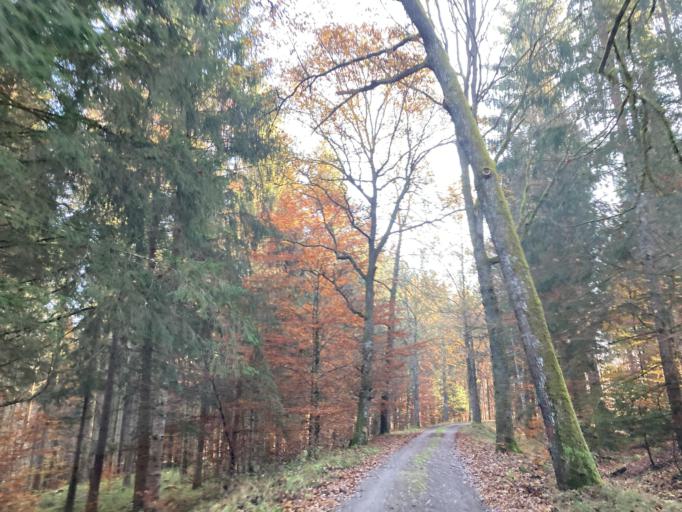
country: DE
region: Baden-Wuerttemberg
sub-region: Regierungsbezirk Stuttgart
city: Hildrizhausen
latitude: 48.5858
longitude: 8.9832
